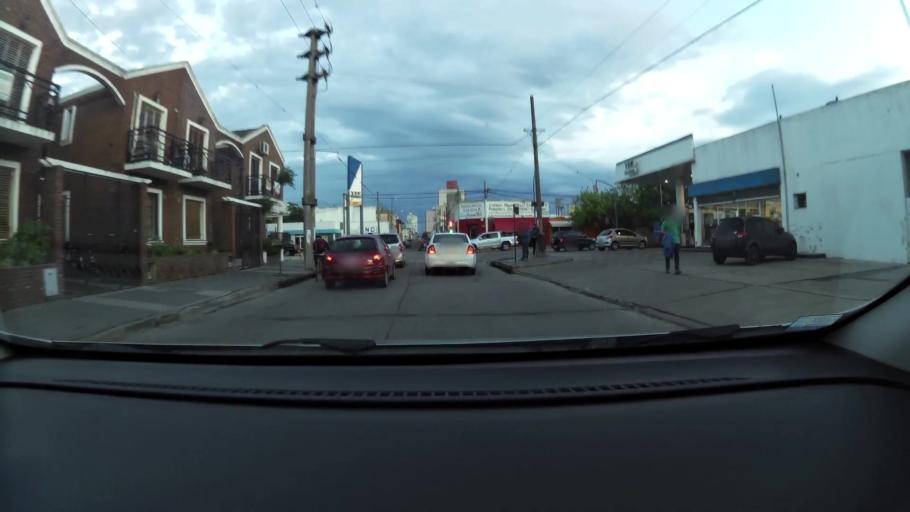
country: AR
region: Buenos Aires
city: San Nicolas de los Arroyos
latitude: -33.3270
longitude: -60.2238
